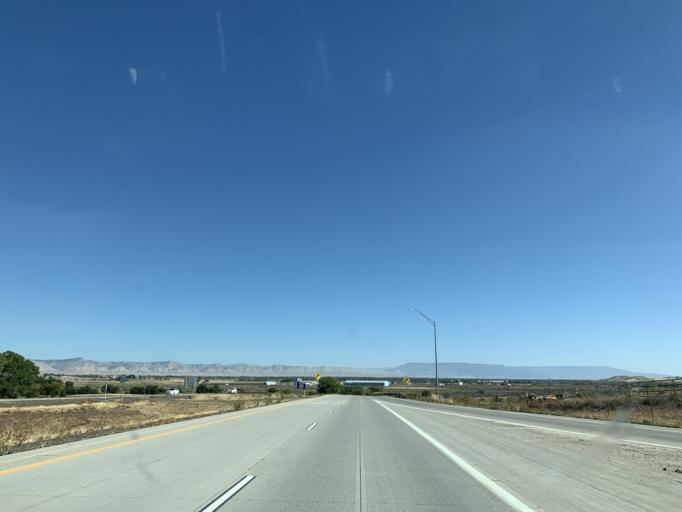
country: US
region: Colorado
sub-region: Mesa County
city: Loma
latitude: 39.1777
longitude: -108.8102
